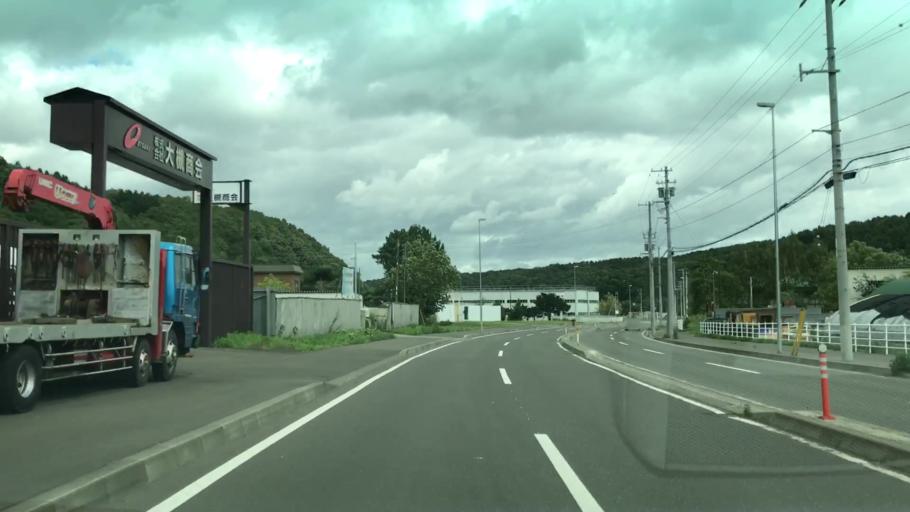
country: JP
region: Hokkaido
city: Kitahiroshima
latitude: 42.9569
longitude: 141.4542
